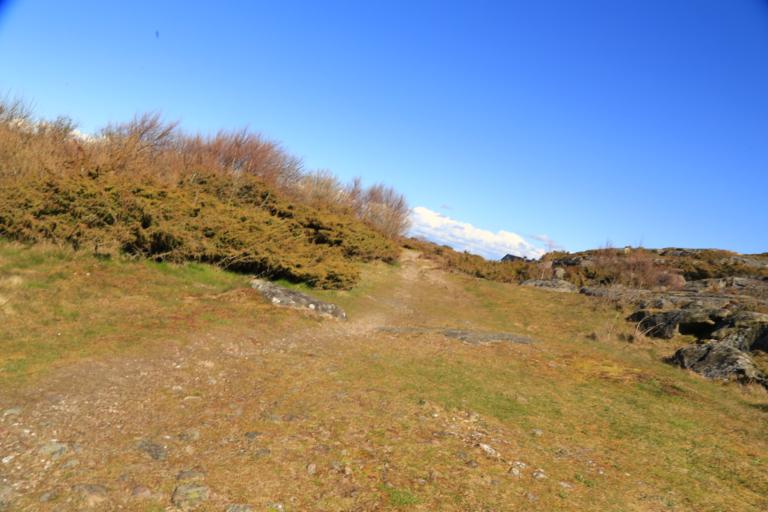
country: SE
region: Halland
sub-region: Varbergs Kommun
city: Varberg
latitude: 57.1194
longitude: 12.1960
